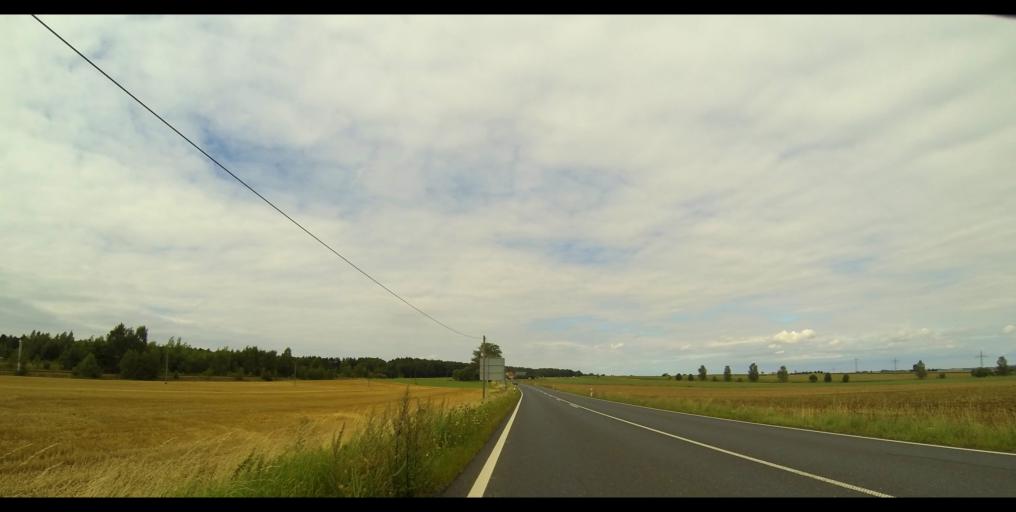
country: DE
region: Saxony
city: Grossschirma
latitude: 50.9959
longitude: 13.2807
